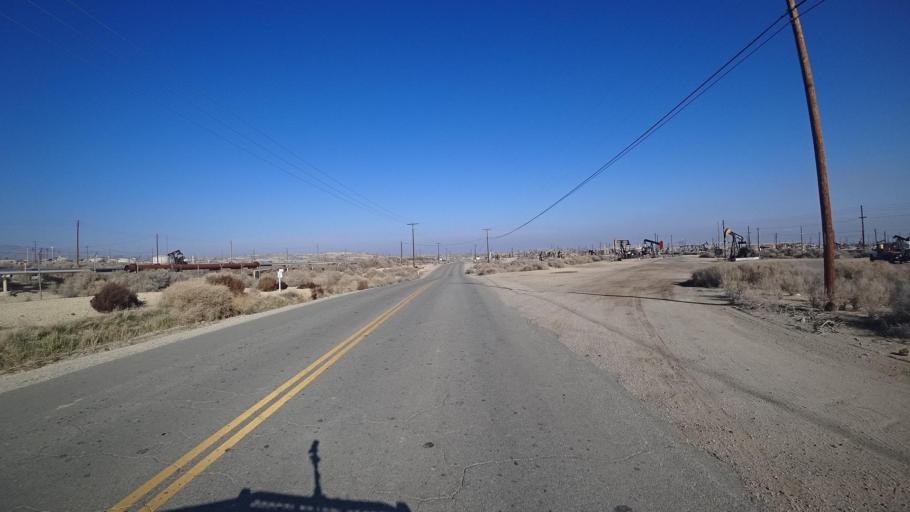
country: US
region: California
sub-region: Kern County
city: Taft Heights
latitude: 35.2116
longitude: -119.5982
